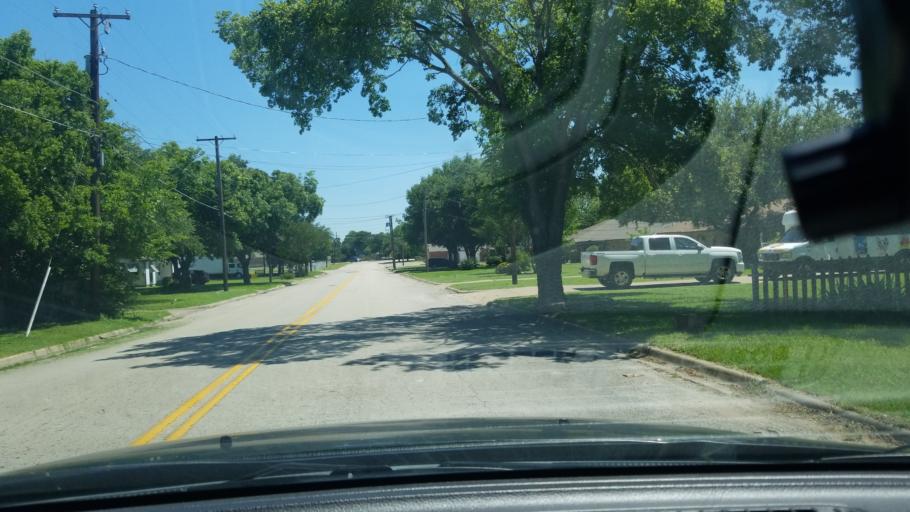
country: US
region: Texas
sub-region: Dallas County
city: Mesquite
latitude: 32.7639
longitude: -96.6044
